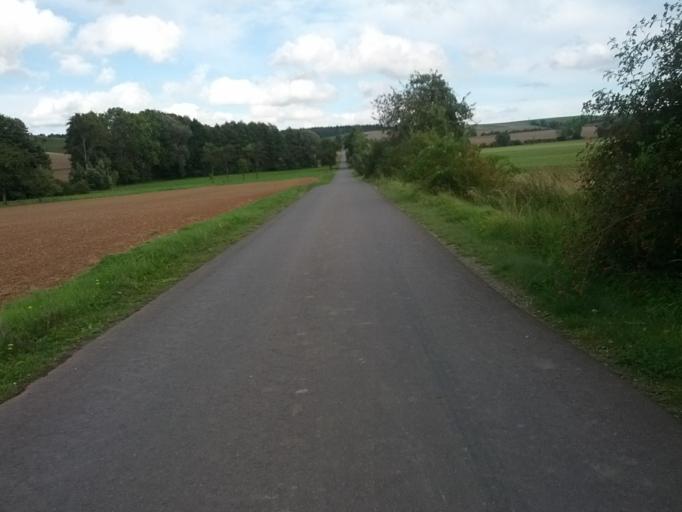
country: DE
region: Thuringia
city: Krauthausen
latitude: 51.0175
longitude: 10.2965
